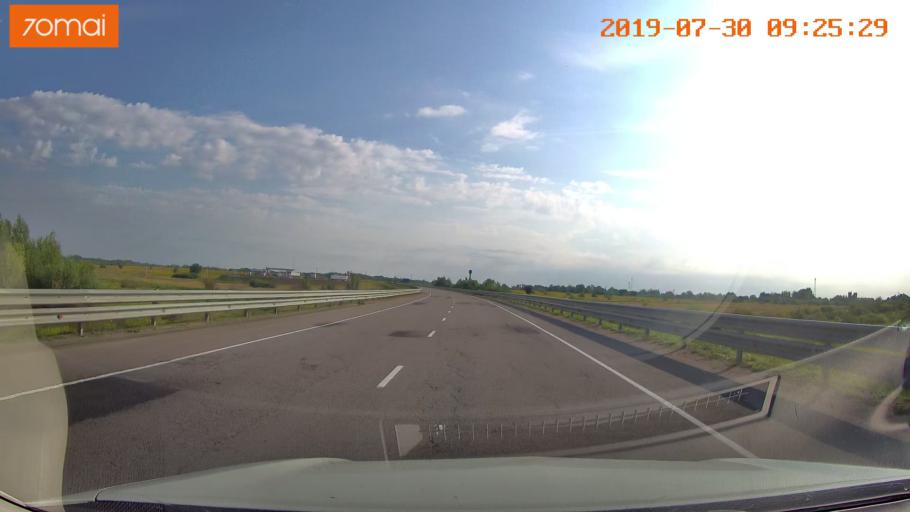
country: LT
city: Kybartai
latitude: 54.6399
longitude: 22.7171
